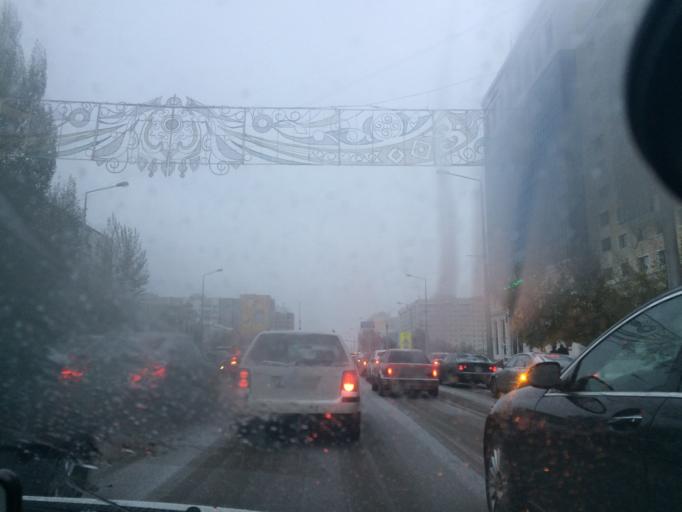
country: KZ
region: Astana Qalasy
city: Astana
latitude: 51.1677
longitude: 71.4083
